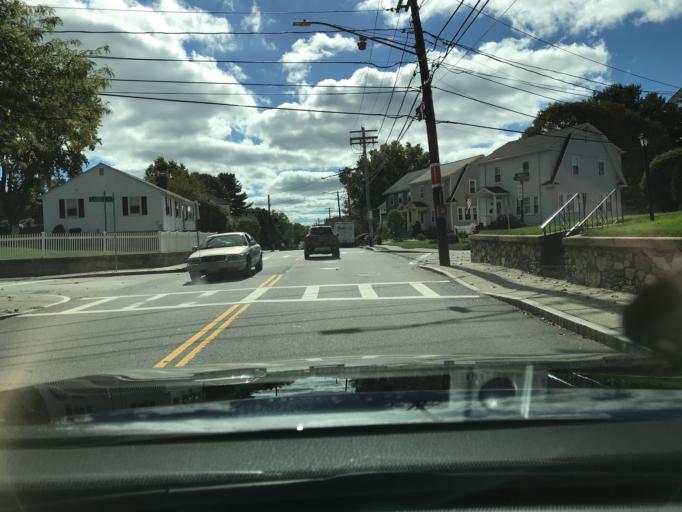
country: US
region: Massachusetts
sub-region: Norfolk County
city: Dedham
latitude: 42.2864
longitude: -71.1709
